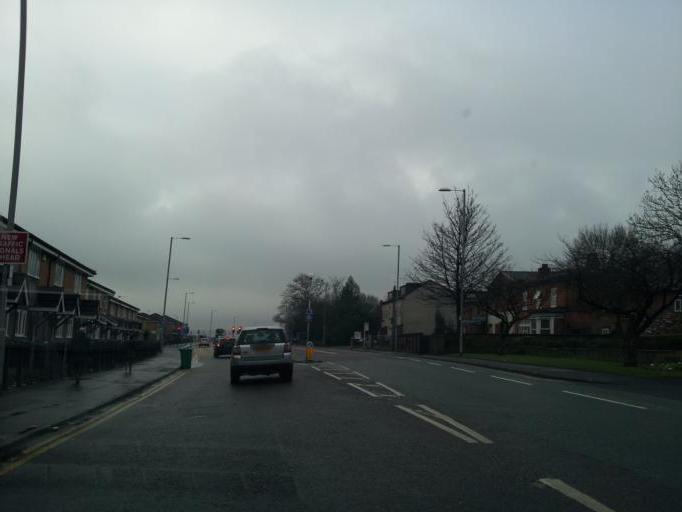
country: GB
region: England
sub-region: Manchester
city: Blackley
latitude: 53.5064
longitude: -2.2177
